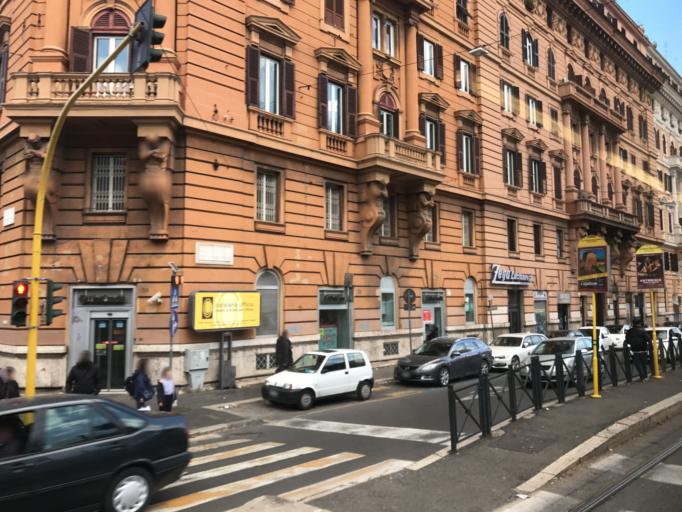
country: IT
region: Latium
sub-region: Citta metropolitana di Roma Capitale
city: Rome
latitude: 41.9129
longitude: 12.5067
